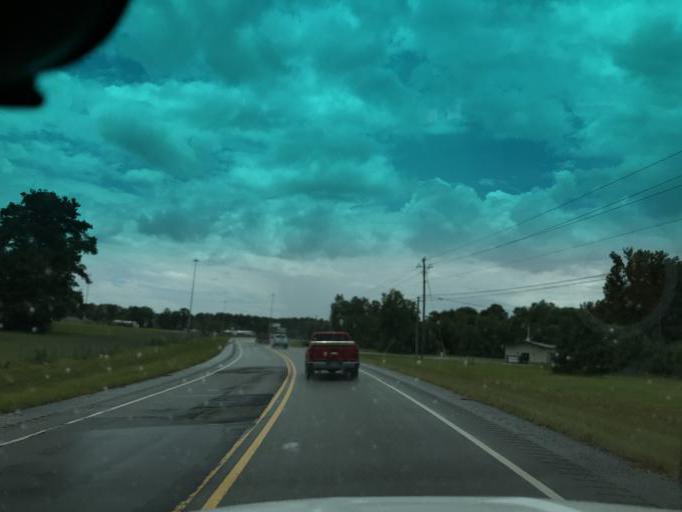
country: US
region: Alabama
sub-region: Montgomery County
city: Pike Road
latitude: 32.3694
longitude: -86.0855
